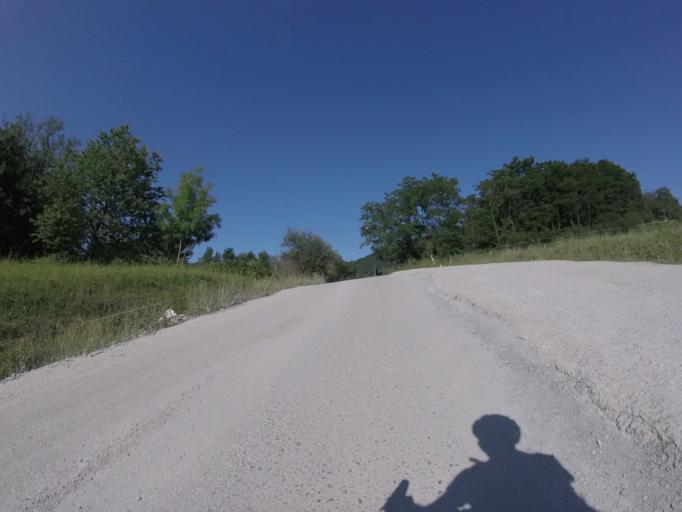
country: ES
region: Basque Country
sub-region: Provincia de Guipuzcoa
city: Astigarraga
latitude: 43.2926
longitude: -1.9365
